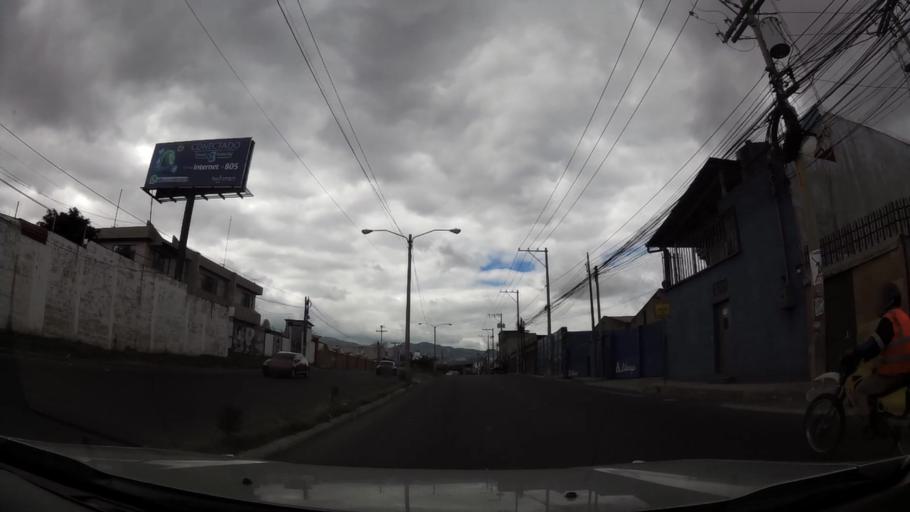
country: GT
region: Guatemala
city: Guatemala City
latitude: 14.6594
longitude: -90.5605
